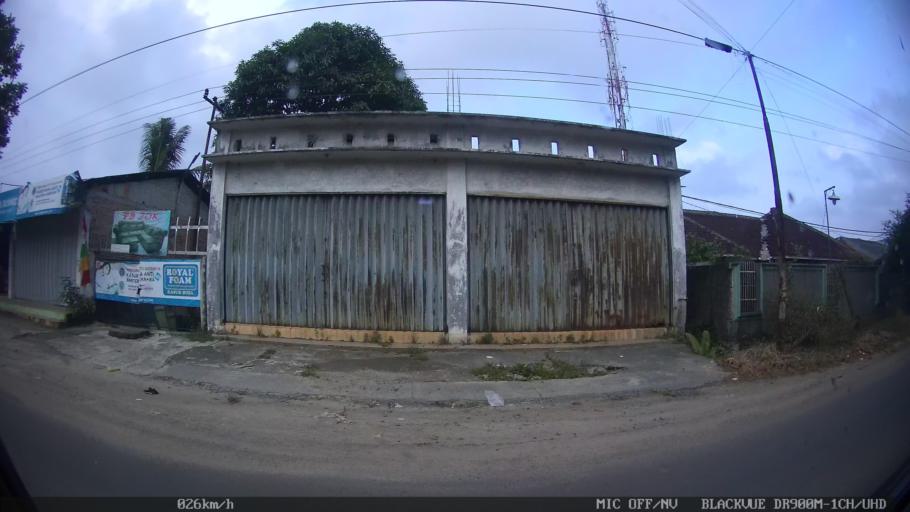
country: ID
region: Lampung
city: Bandarlampung
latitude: -5.4160
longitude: 105.2857
